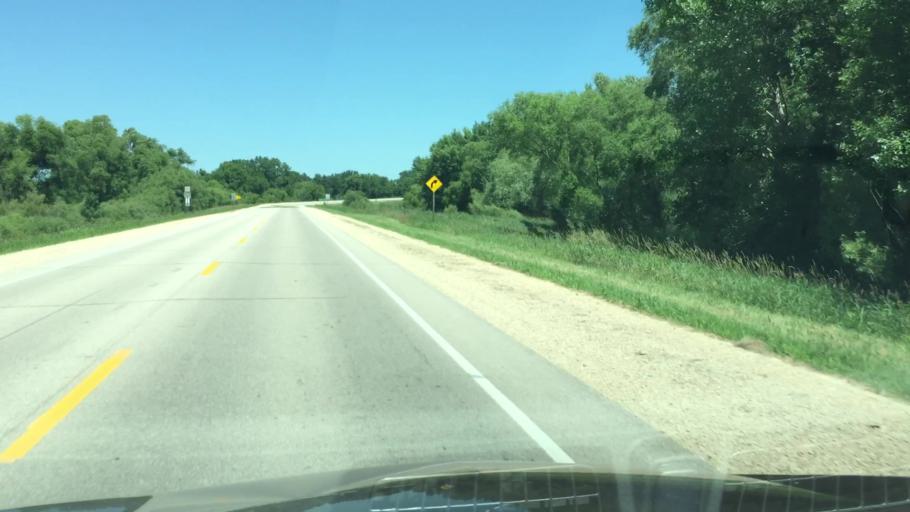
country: US
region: Iowa
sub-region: Cedar County
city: Mechanicsville
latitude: 42.0031
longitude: -91.1418
